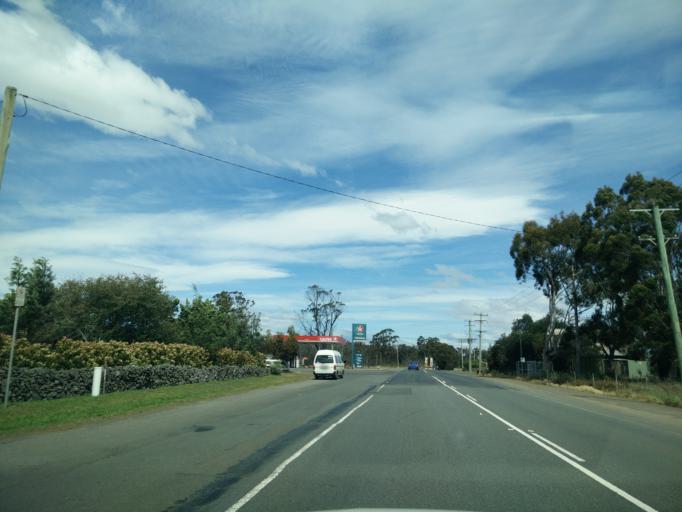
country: AU
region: Tasmania
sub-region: Northern Midlands
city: Evandale
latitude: -41.7591
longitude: 147.3504
